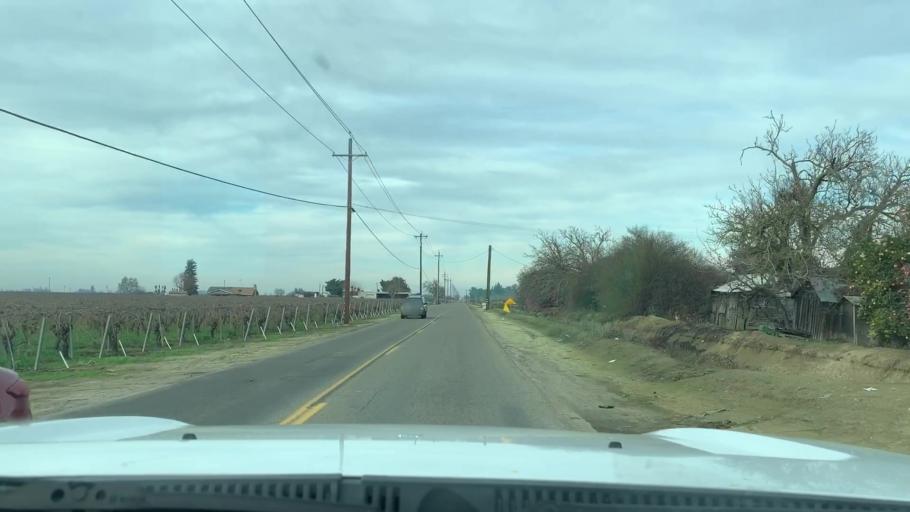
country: US
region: California
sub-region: Fresno County
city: Selma
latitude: 36.5689
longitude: -119.5750
